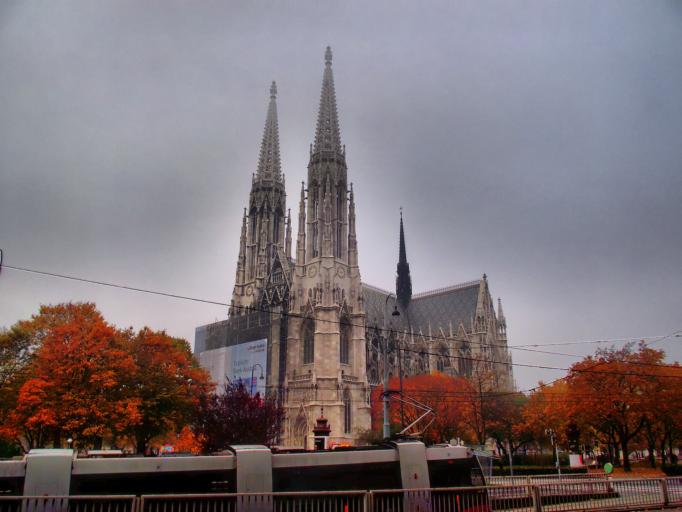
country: AT
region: Vienna
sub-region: Wien Stadt
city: Vienna
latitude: 48.2155
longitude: 16.3611
